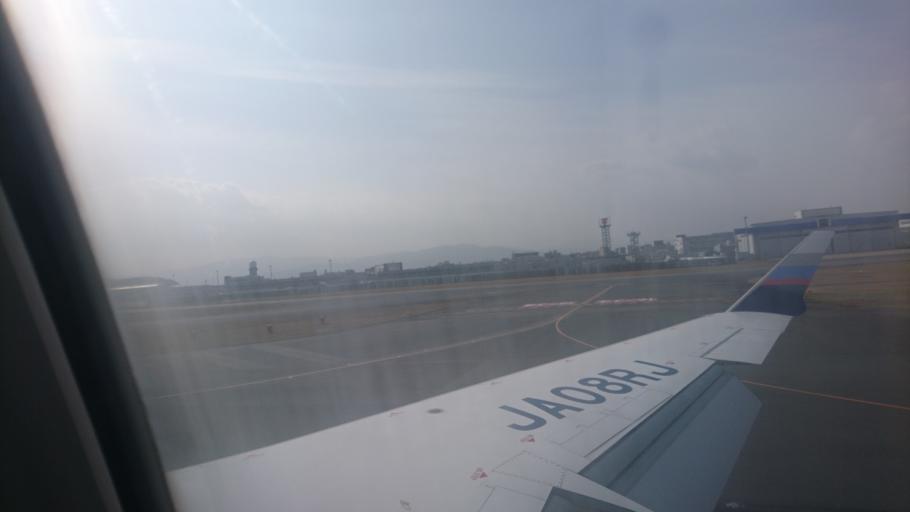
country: JP
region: Fukuoka
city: Fukuoka-shi
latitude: 33.5932
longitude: 130.4457
